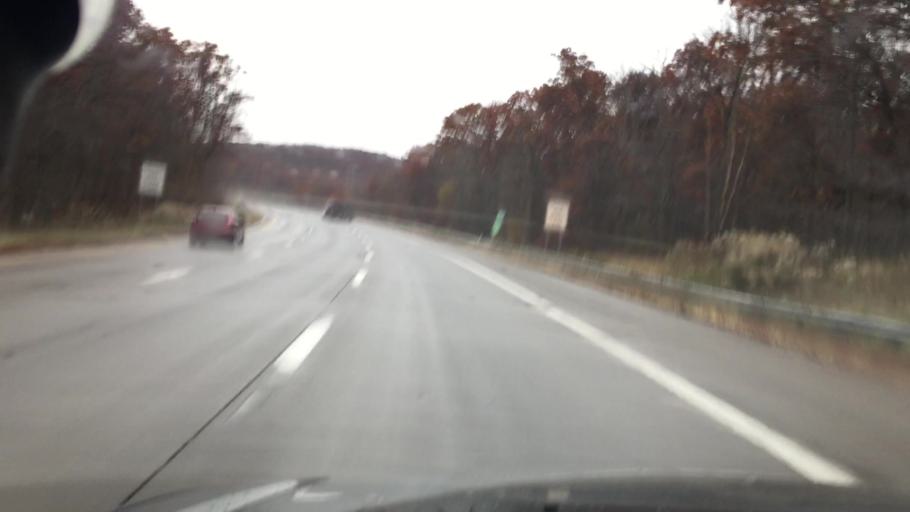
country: US
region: Pennsylvania
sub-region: Luzerne County
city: Nanticoke
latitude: 41.1604
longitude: -75.9550
